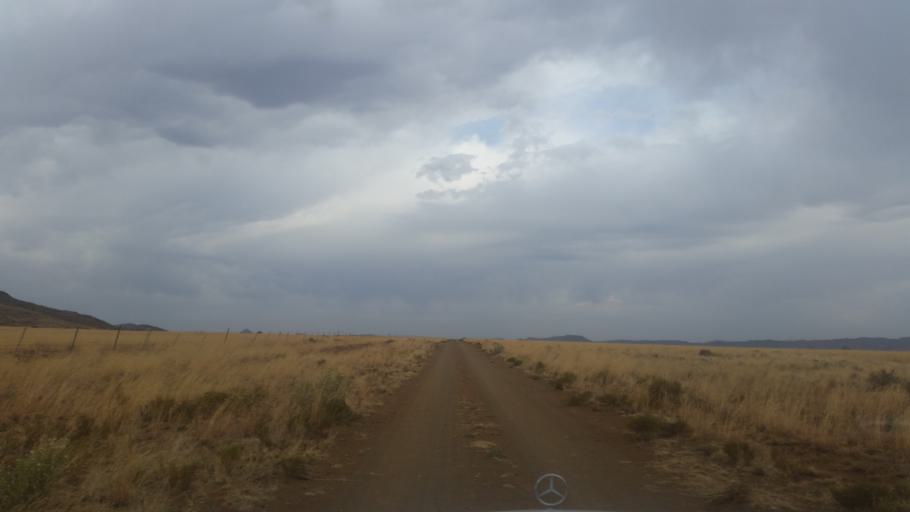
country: ZA
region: Orange Free State
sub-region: Xhariep District Municipality
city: Trompsburg
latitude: -30.5070
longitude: 25.9211
